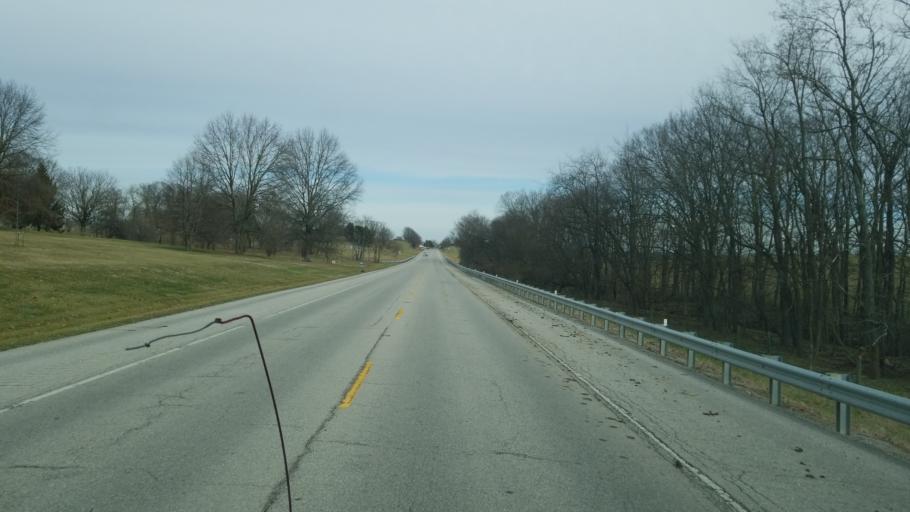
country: US
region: Kentucky
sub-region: Fleming County
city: Flemingsburg
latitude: 38.5107
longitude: -83.8448
